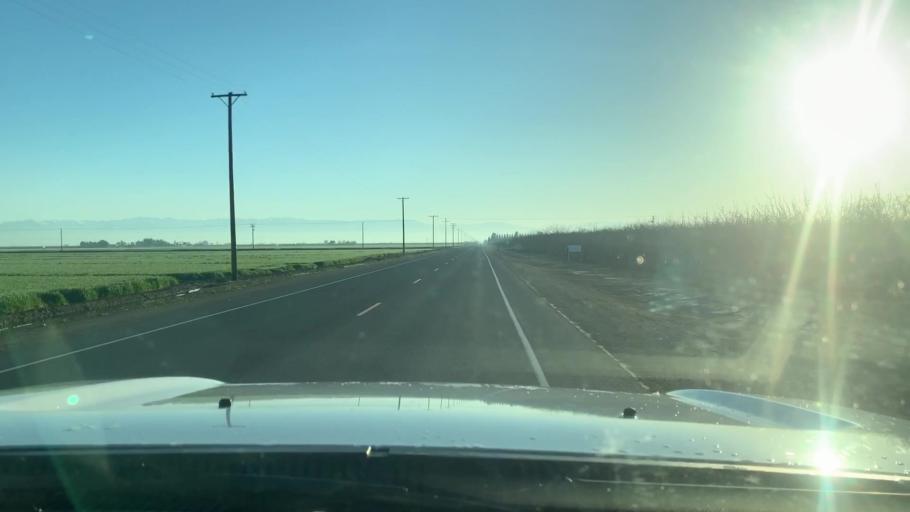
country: US
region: California
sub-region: Kings County
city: Corcoran
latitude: 36.2110
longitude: -119.5145
